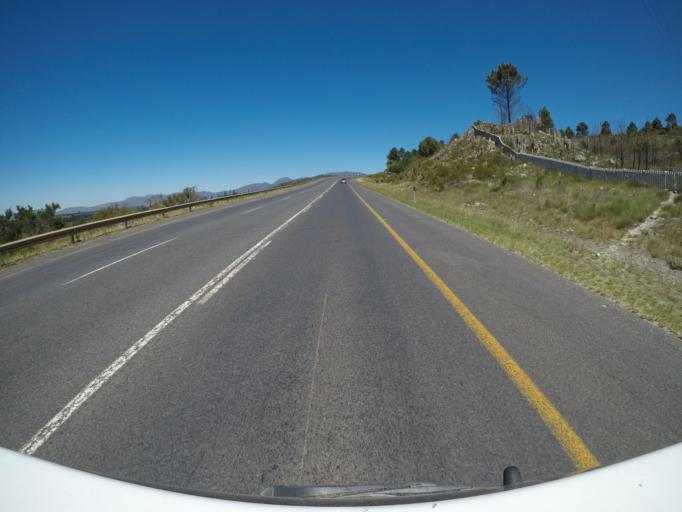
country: ZA
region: Western Cape
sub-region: Overberg District Municipality
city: Grabouw
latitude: -34.1655
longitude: 19.0031
